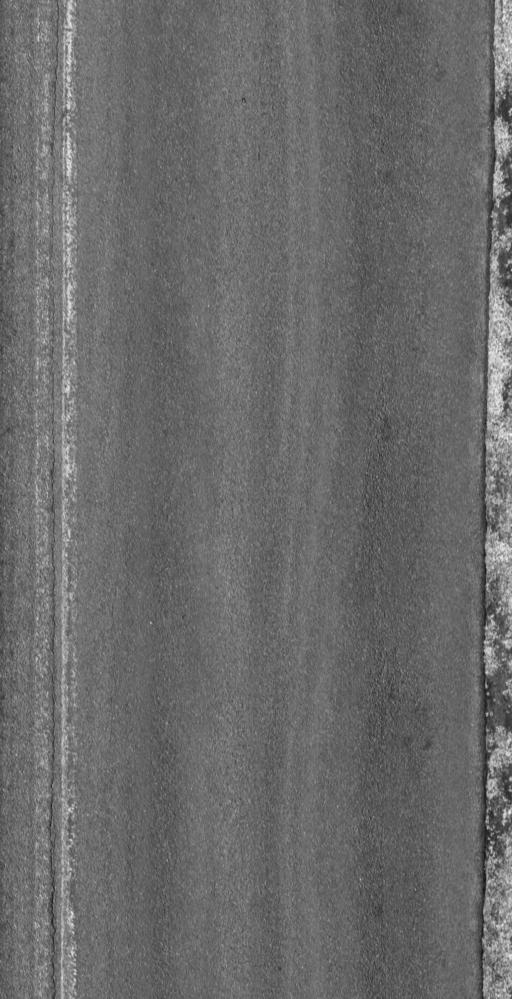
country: US
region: Vermont
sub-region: Chittenden County
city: South Burlington
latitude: 44.4094
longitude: -73.1406
